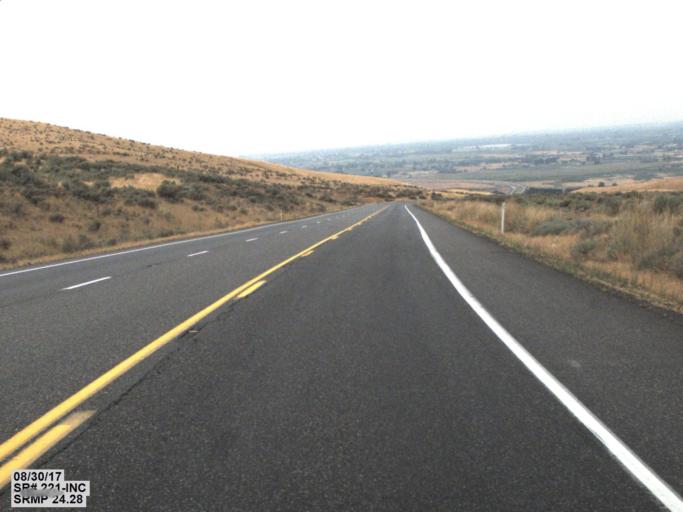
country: US
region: Washington
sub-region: Benton County
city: Prosser
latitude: 46.1998
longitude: -119.7191
